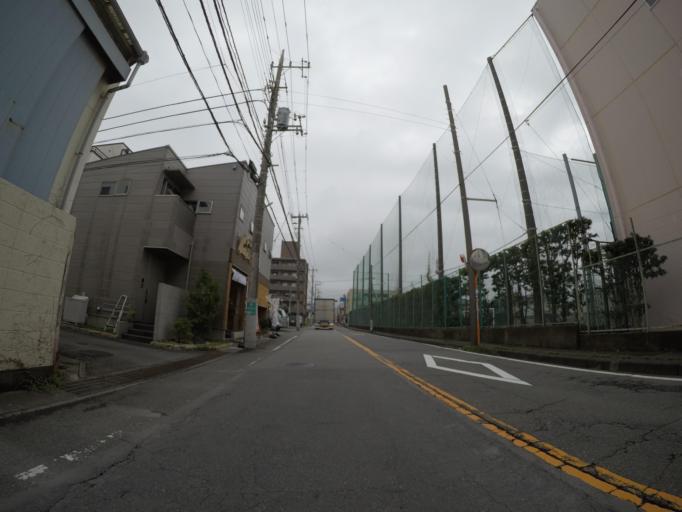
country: JP
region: Shizuoka
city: Numazu
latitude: 35.1135
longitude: 138.8524
